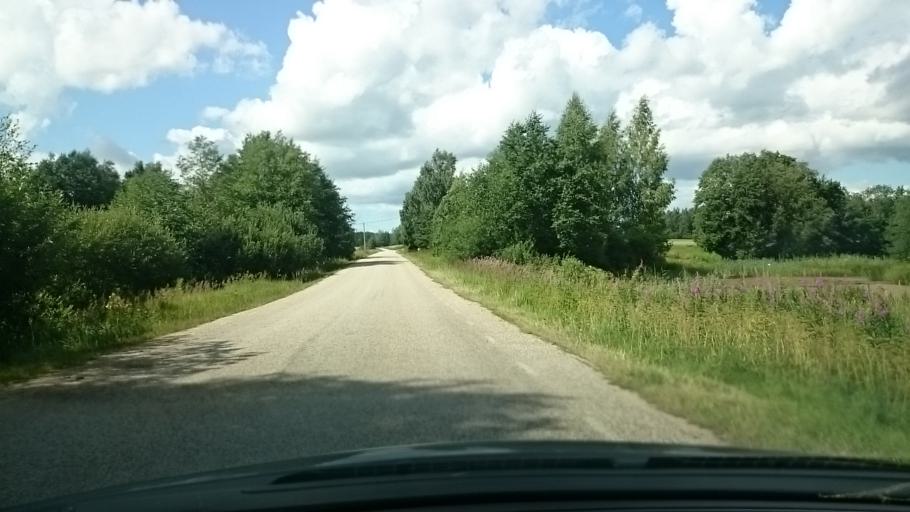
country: EE
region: Vorumaa
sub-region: Voru linn
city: Voru
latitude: 57.9153
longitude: 27.1761
